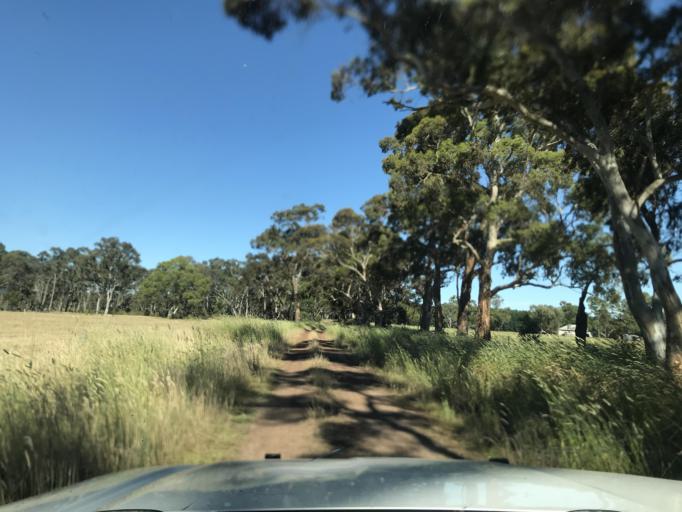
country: AU
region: South Australia
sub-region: Wattle Range
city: Penola
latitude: -37.0800
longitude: 141.3789
